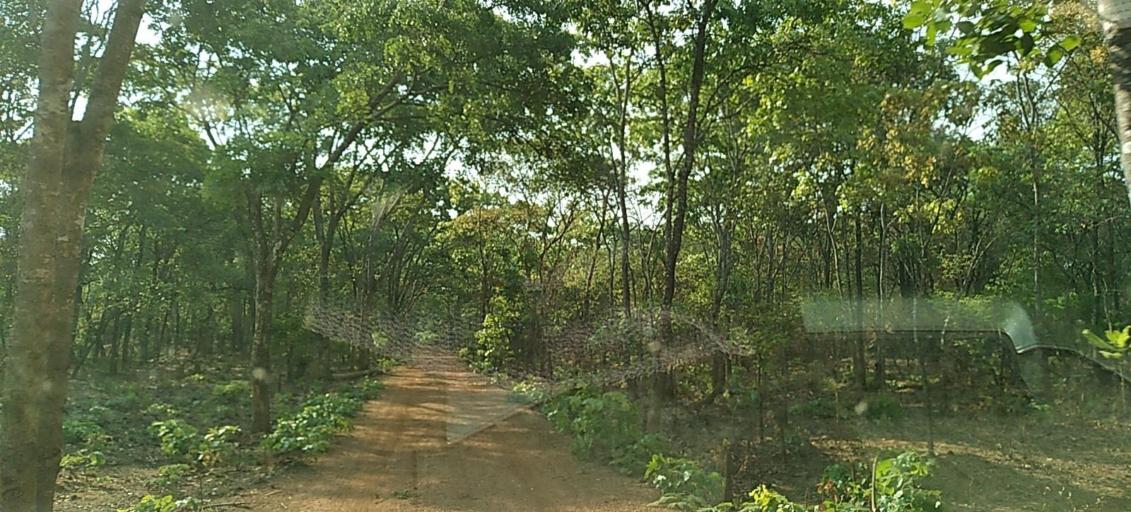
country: ZM
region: Copperbelt
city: Kalulushi
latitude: -13.0003
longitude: 27.7109
